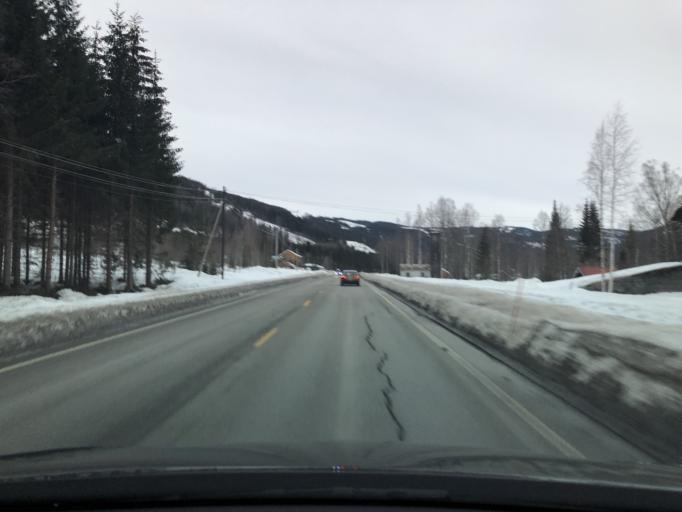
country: NO
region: Oppland
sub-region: Etnedal
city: Bruflat
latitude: 60.6474
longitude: 9.7961
